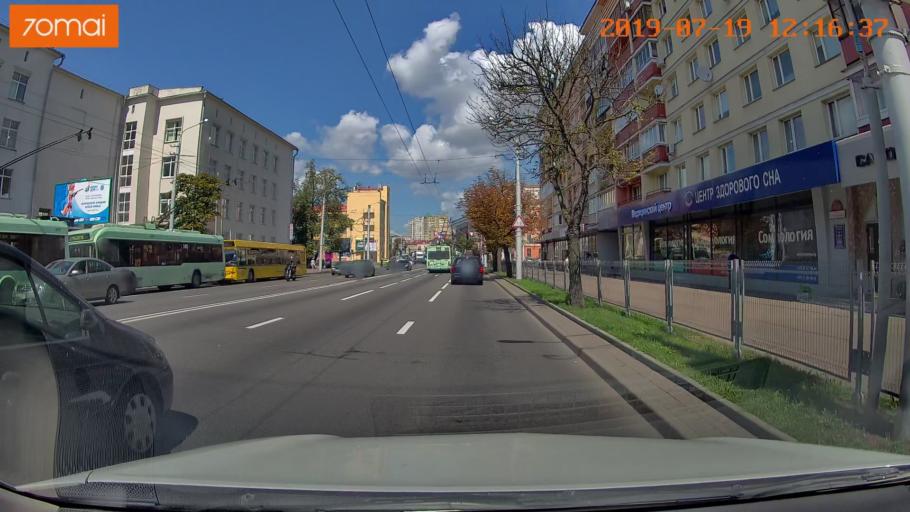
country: BY
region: Minsk
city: Minsk
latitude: 53.9213
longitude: 27.6018
